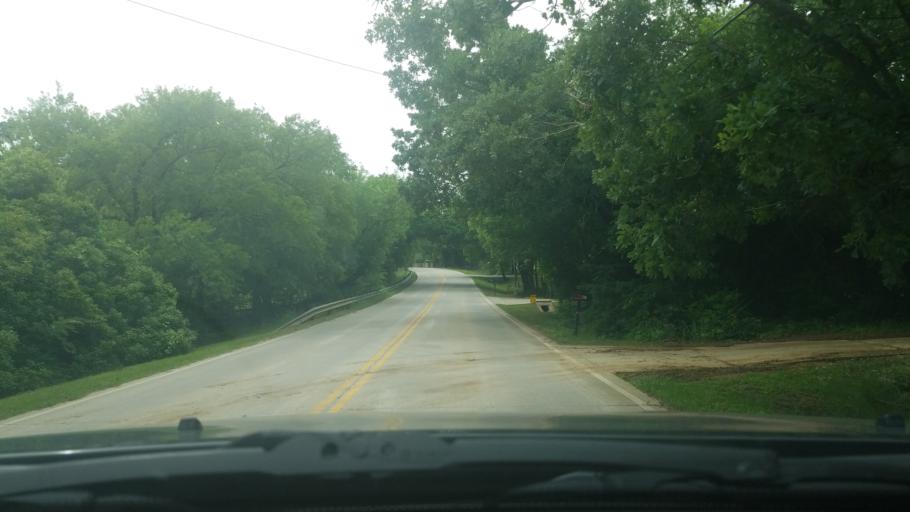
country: US
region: Texas
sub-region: Denton County
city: Lake Dallas
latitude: 33.1122
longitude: -97.0188
